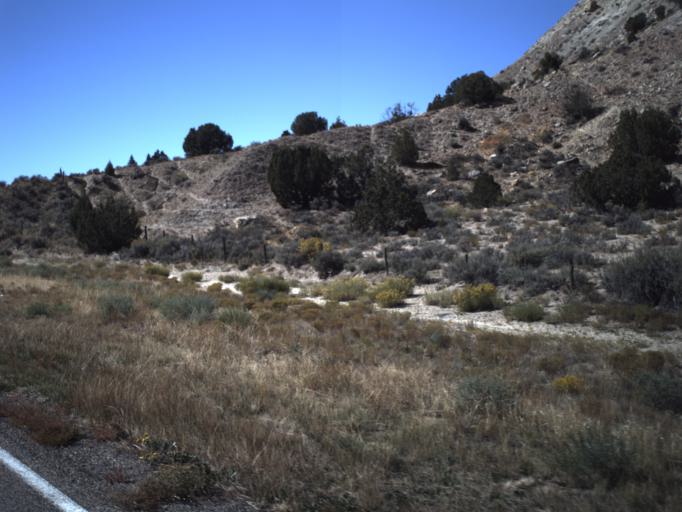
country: US
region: Utah
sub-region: Garfield County
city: Panguitch
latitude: 37.5589
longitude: -112.0186
